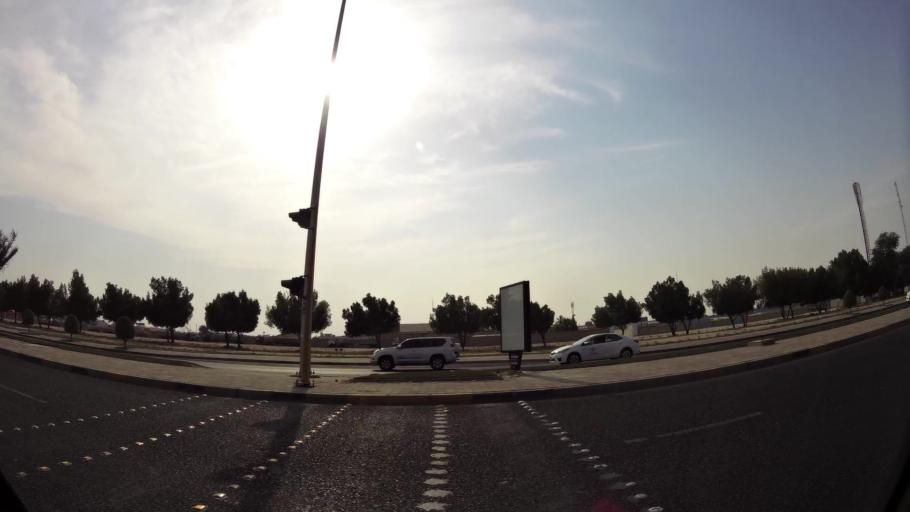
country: KW
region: Al Asimah
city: Ash Shamiyah
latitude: 29.3268
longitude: 47.9565
